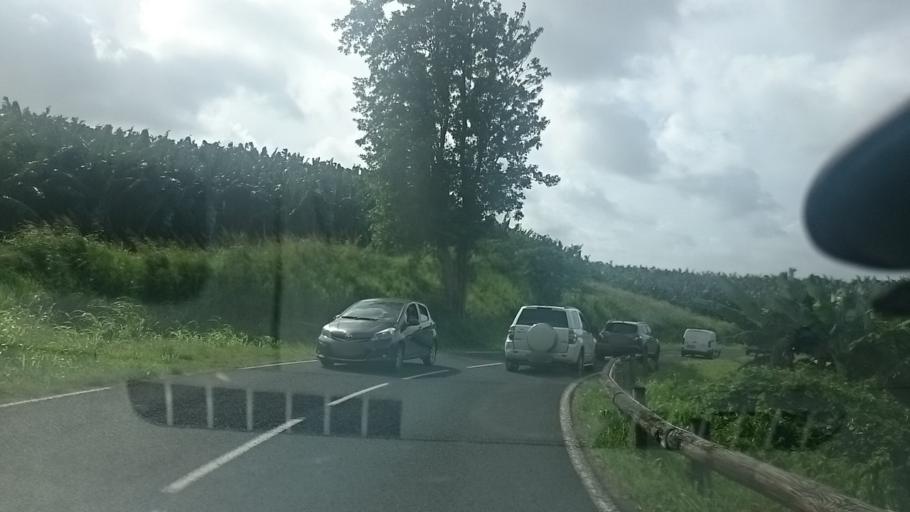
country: MQ
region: Martinique
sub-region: Martinique
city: Le Francois
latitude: 14.5975
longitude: -60.9108
